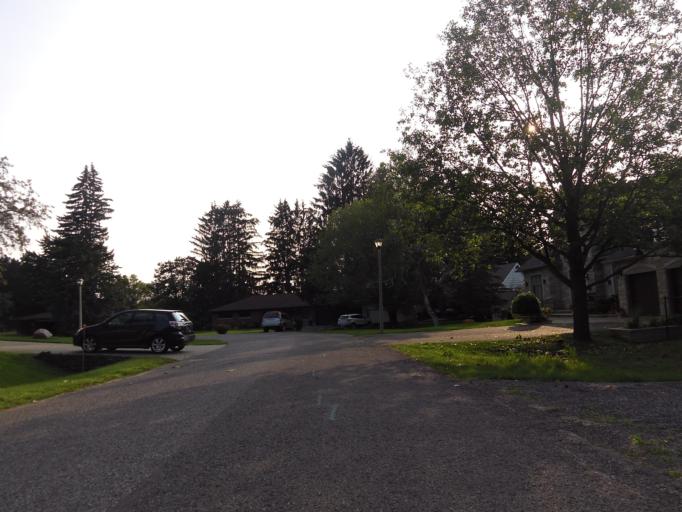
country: CA
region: Ontario
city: Ottawa
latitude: 45.3538
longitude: -75.6972
